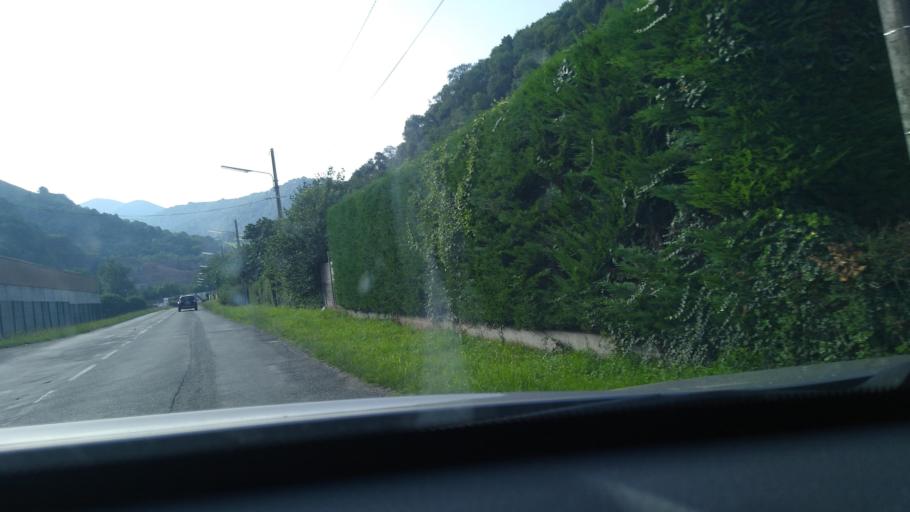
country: FR
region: Midi-Pyrenees
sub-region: Departement de l'Ariege
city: Saint-Girons
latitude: 42.9676
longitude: 1.1656
